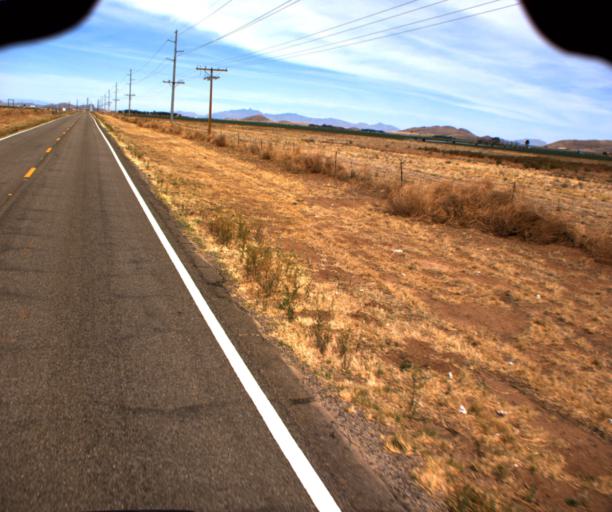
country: US
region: Arizona
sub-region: Cochise County
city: Tombstone
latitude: 31.8085
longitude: -109.6941
